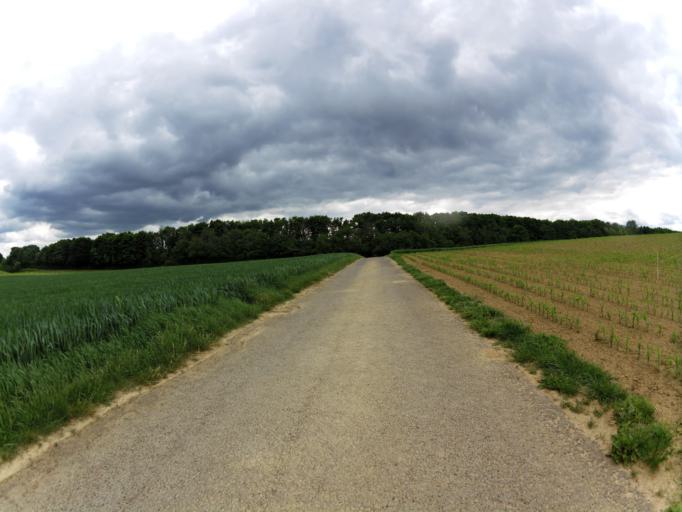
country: DE
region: Bavaria
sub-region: Regierungsbezirk Unterfranken
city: Gaukonigshofen
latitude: 49.6614
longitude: 9.9995
